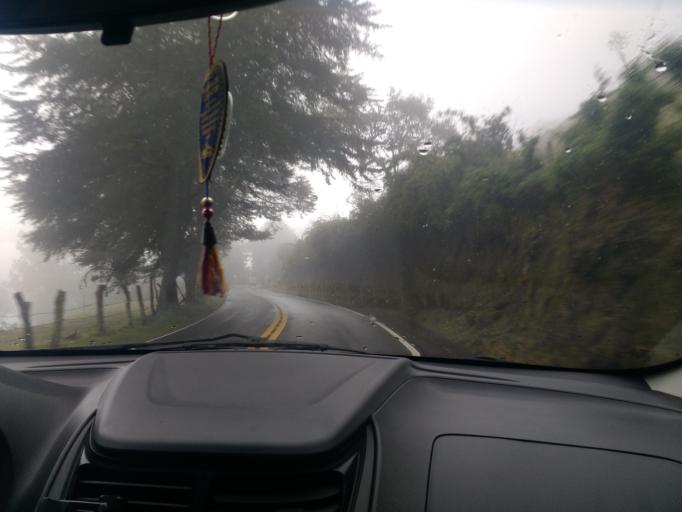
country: CO
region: Cundinamarca
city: Choachi
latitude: 4.5658
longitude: -73.9619
